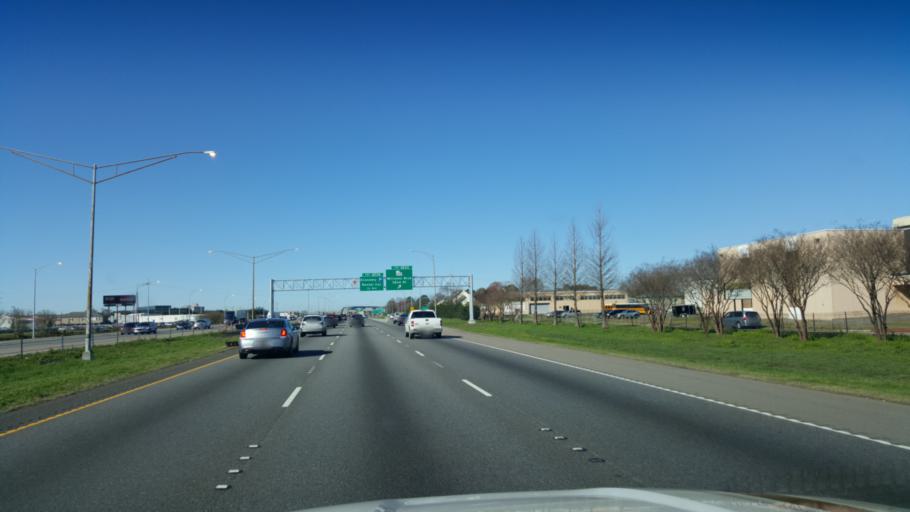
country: US
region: Louisiana
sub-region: Jefferson Parish
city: Kenner
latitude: 30.0076
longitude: -90.2251
